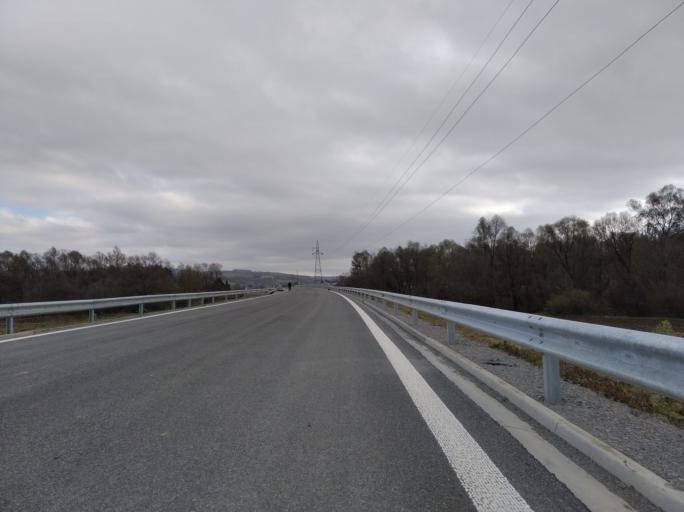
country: PL
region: Subcarpathian Voivodeship
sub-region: Powiat strzyzowski
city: Strzyzow
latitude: 49.8650
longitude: 21.7760
